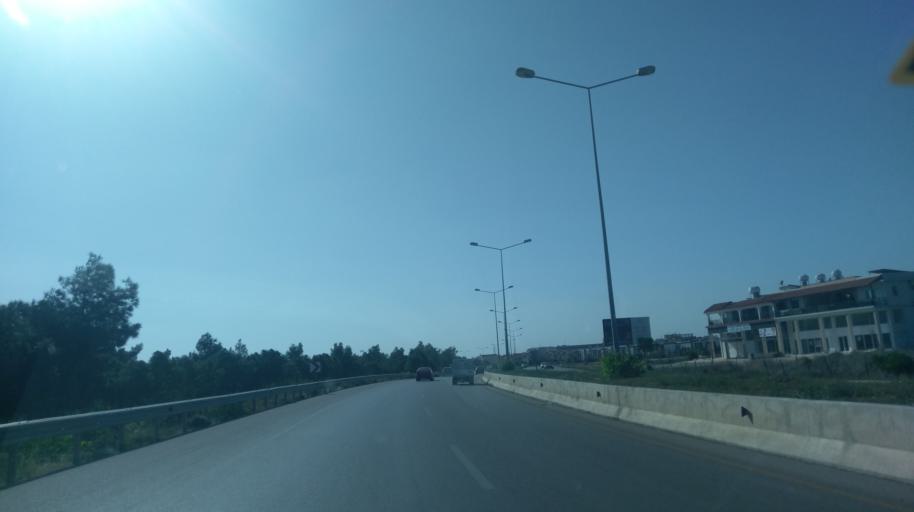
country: CY
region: Ammochostos
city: Trikomo
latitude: 35.2003
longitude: 33.8945
